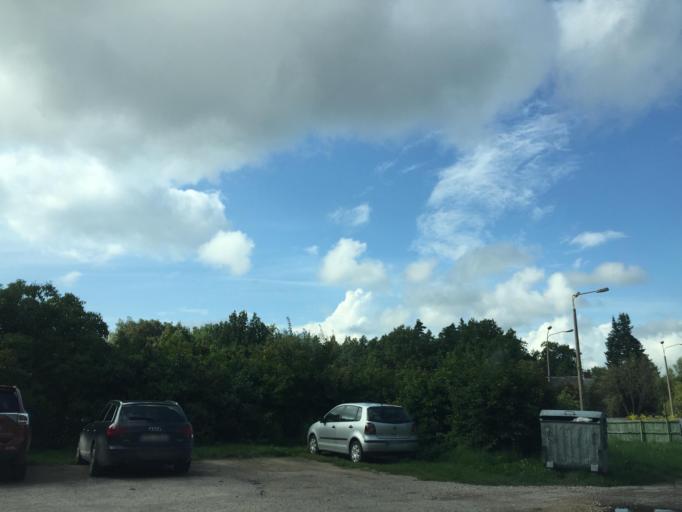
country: LV
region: Priekuli
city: Priekuli
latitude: 57.3533
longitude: 25.3315
